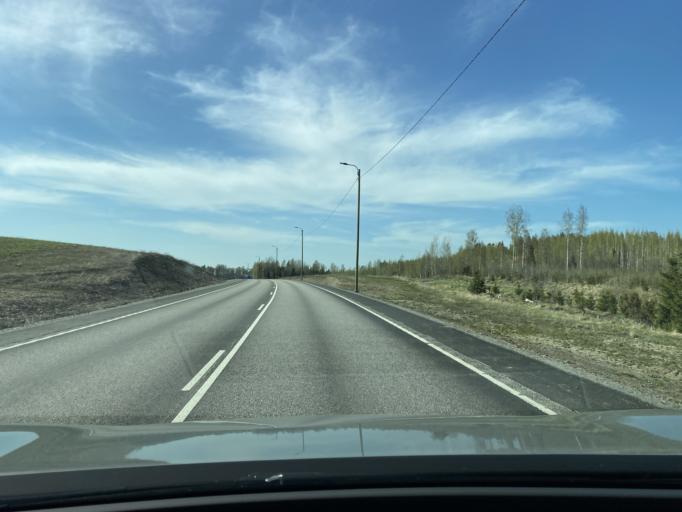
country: FI
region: Uusimaa
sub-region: Helsinki
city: Nurmijaervi
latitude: 60.4210
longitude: 24.7371
